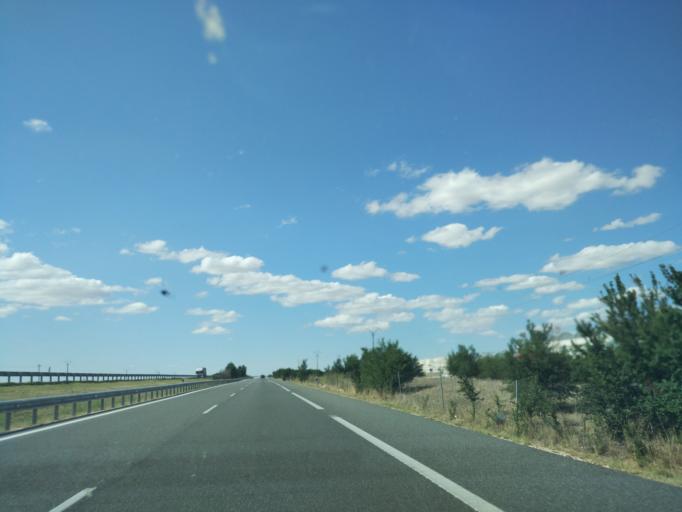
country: ES
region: Castille and Leon
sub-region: Provincia de Valladolid
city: San Vicente del Palacio
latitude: 41.2547
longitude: -4.8735
